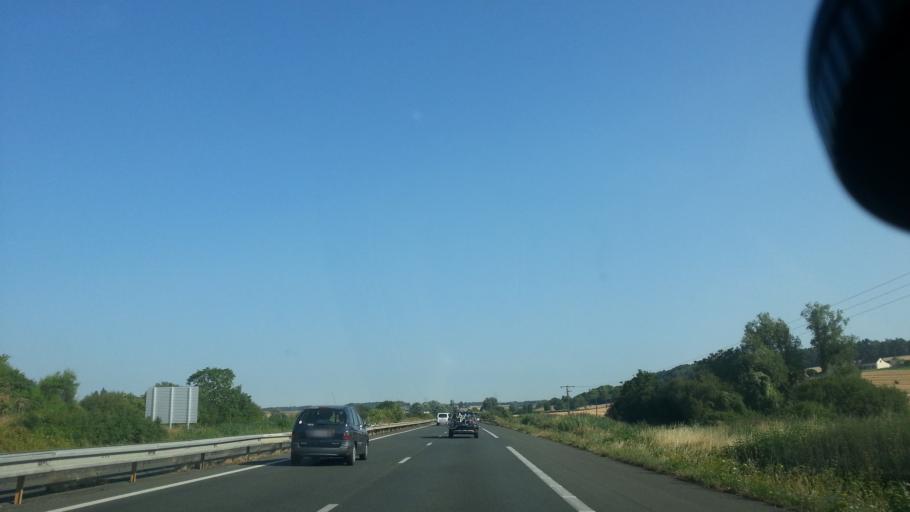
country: FR
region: Poitou-Charentes
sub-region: Departement de la Vienne
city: Antran
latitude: 46.8693
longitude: 0.5227
